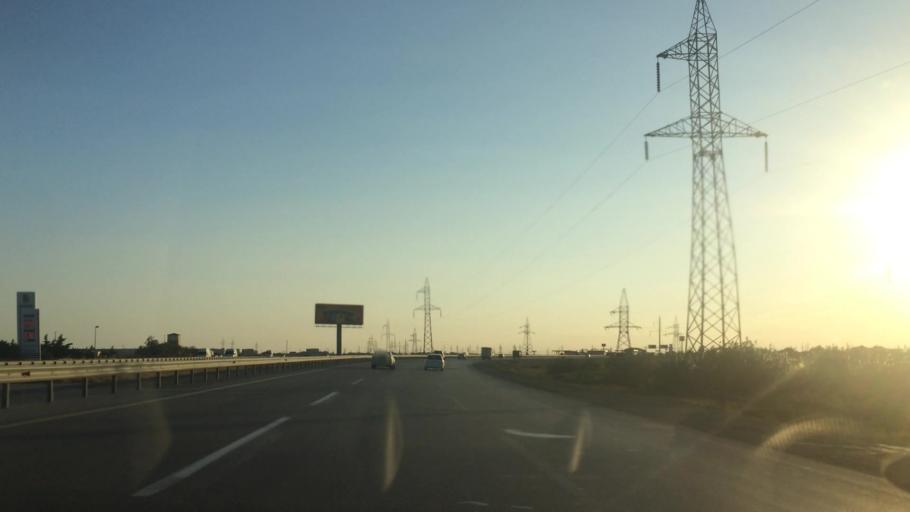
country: AZ
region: Baki
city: Qobustan
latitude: 39.9709
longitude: 49.4150
